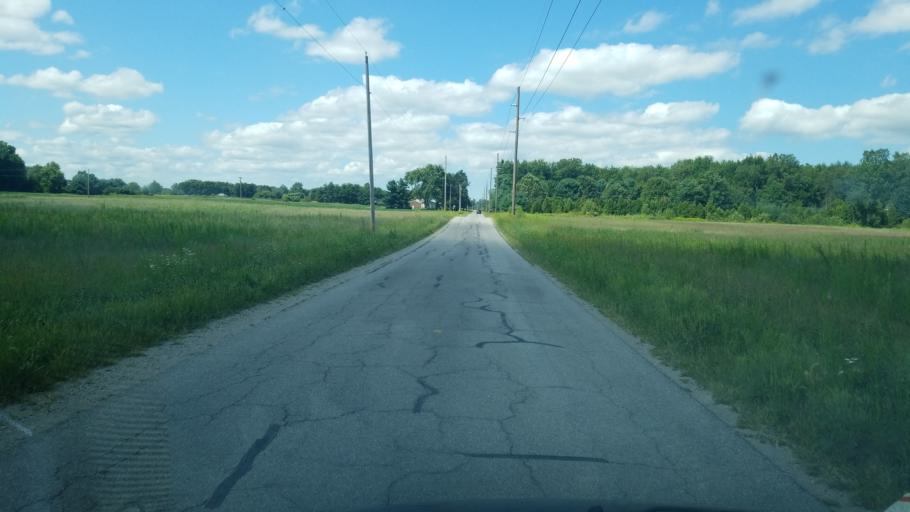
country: US
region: Ohio
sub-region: Lucas County
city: Whitehouse
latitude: 41.4513
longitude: -83.8891
